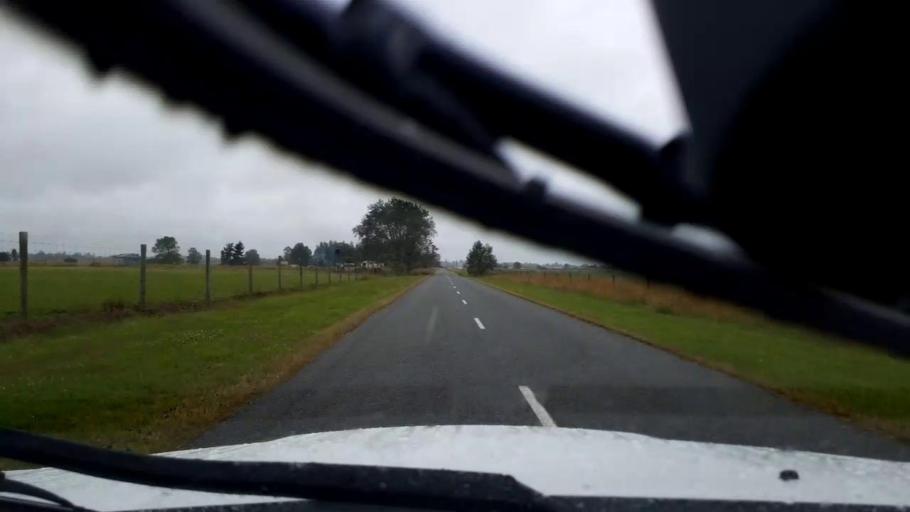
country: NZ
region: Canterbury
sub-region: Timaru District
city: Pleasant Point
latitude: -44.2517
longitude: 171.2248
